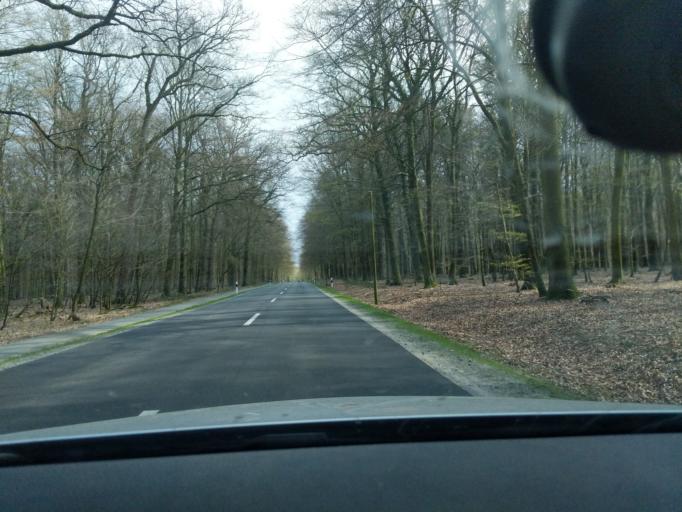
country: DE
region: Lower Saxony
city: Dollern
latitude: 53.5197
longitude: 9.5015
